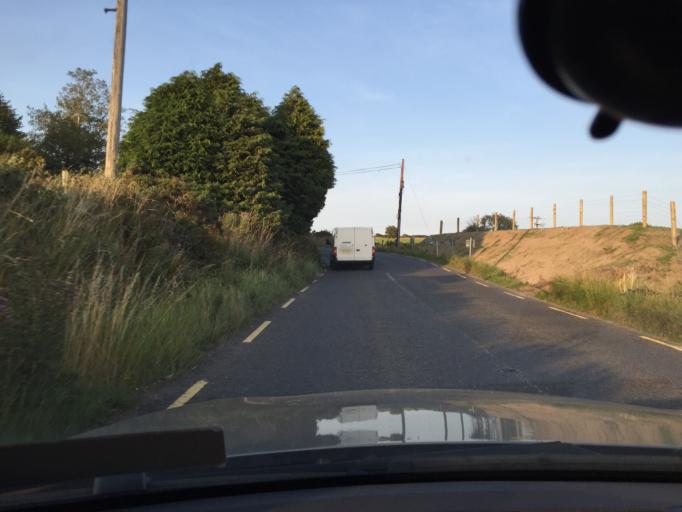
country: IE
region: Leinster
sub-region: Wicklow
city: Kilmacanoge
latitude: 53.1305
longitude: -6.1777
